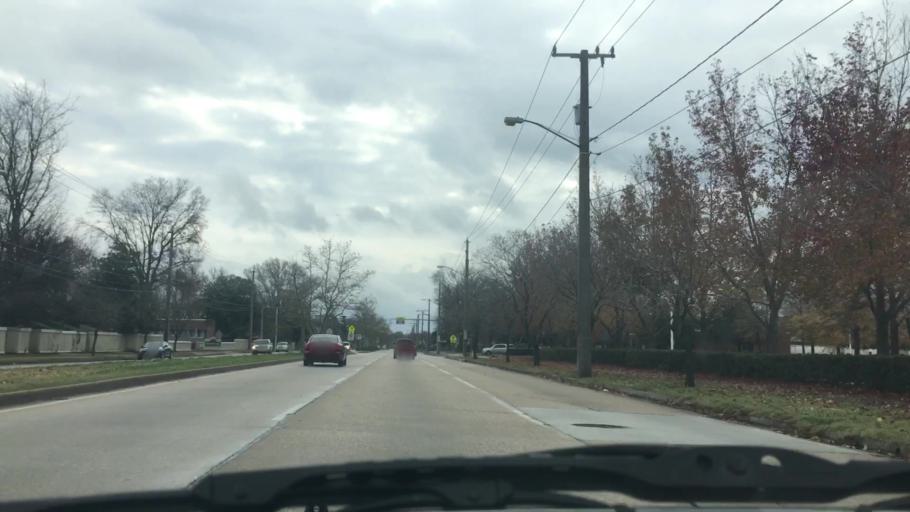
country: US
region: Virginia
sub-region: City of Norfolk
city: Norfolk
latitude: 36.8994
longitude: -76.2391
